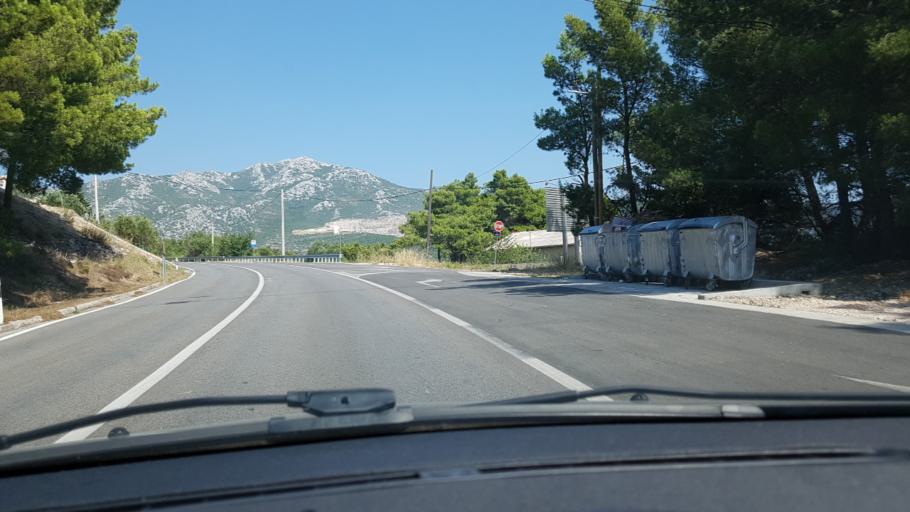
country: HR
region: Splitsko-Dalmatinska
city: Klis
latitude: 43.5563
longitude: 16.5096
